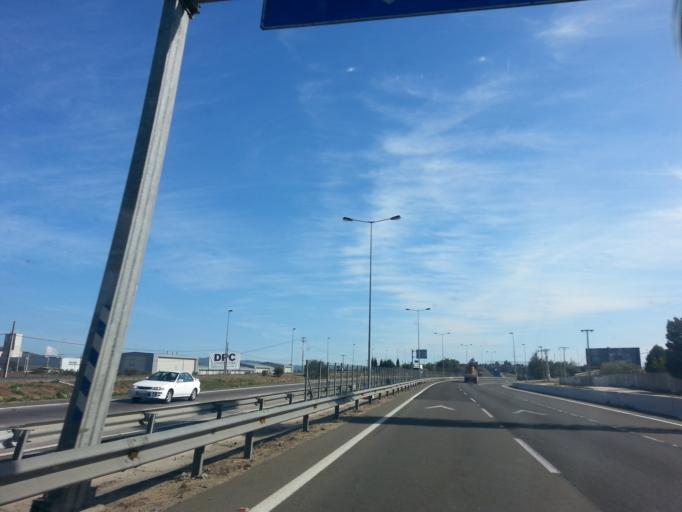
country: CL
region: Valparaiso
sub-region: Provincia de Marga Marga
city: Villa Alemana
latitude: -33.3318
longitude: -71.3858
